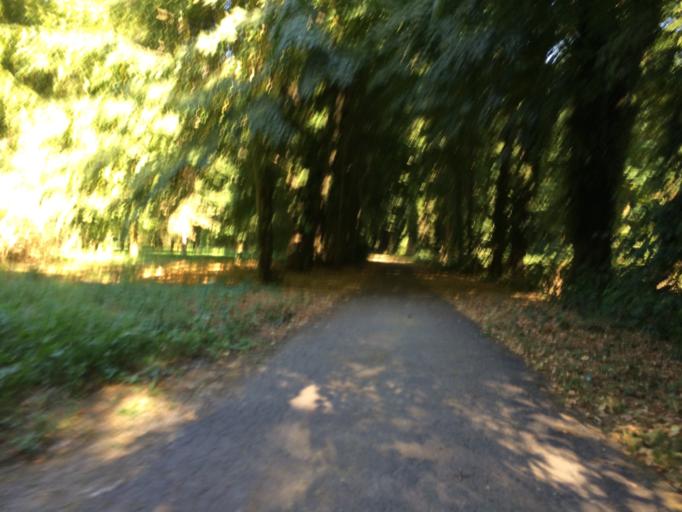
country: FR
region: Ile-de-France
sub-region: Departement de l'Essonne
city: Palaiseau
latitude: 48.7352
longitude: 2.2475
